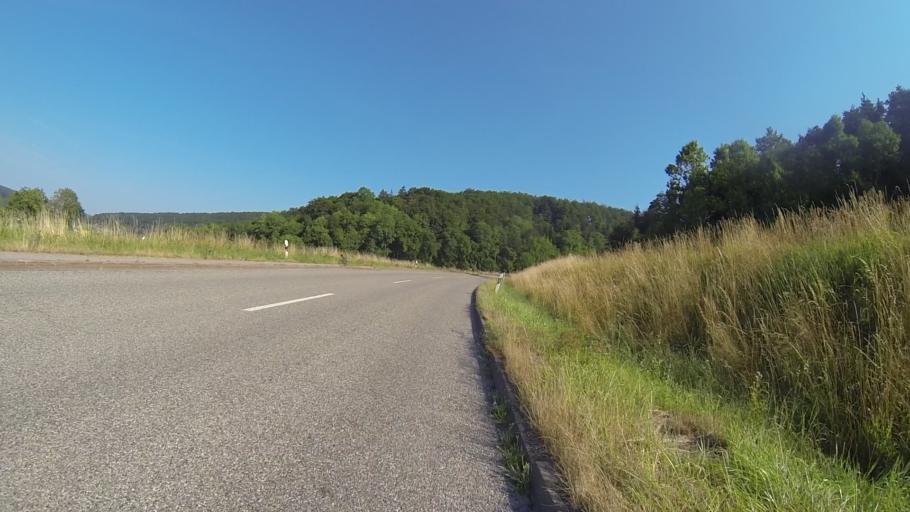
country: DE
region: Baden-Wuerttemberg
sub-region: Regierungsbezirk Stuttgart
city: Konigsbronn
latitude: 48.7348
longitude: 10.1378
